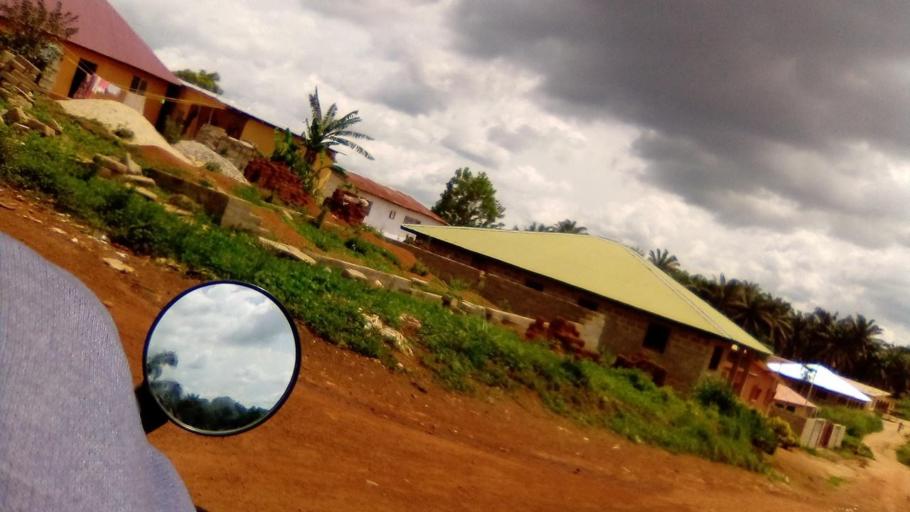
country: SL
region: Southern Province
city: Bo
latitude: 7.9667
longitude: -11.7207
